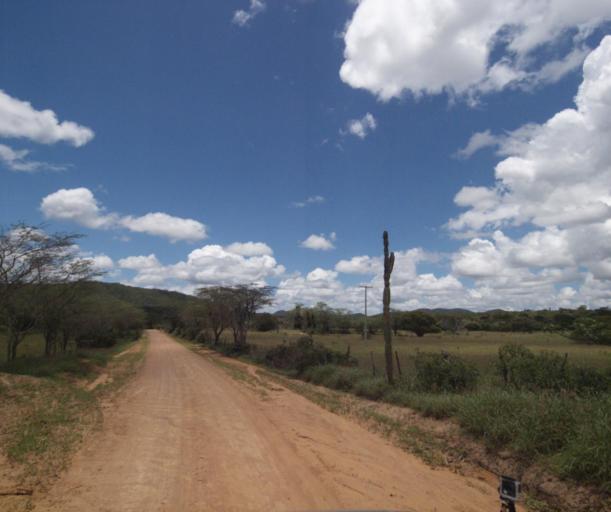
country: BR
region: Bahia
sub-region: Pocoes
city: Pocoes
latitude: -14.3807
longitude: -40.3771
